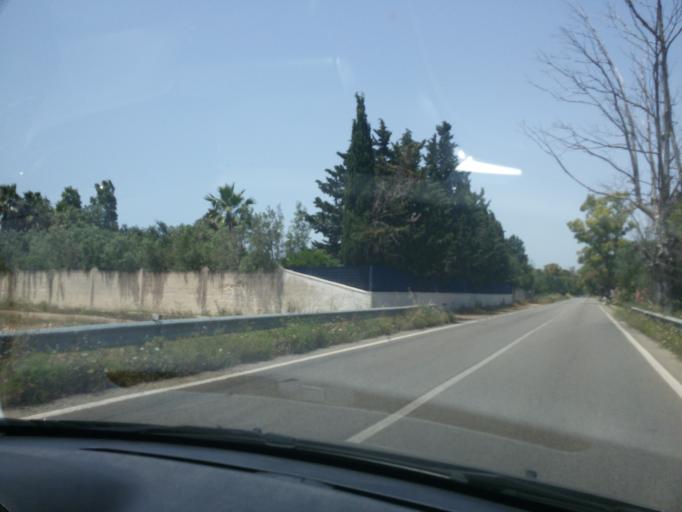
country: IT
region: Apulia
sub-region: Provincia di Lecce
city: Porto Cesareo
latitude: 40.2586
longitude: 17.9241
